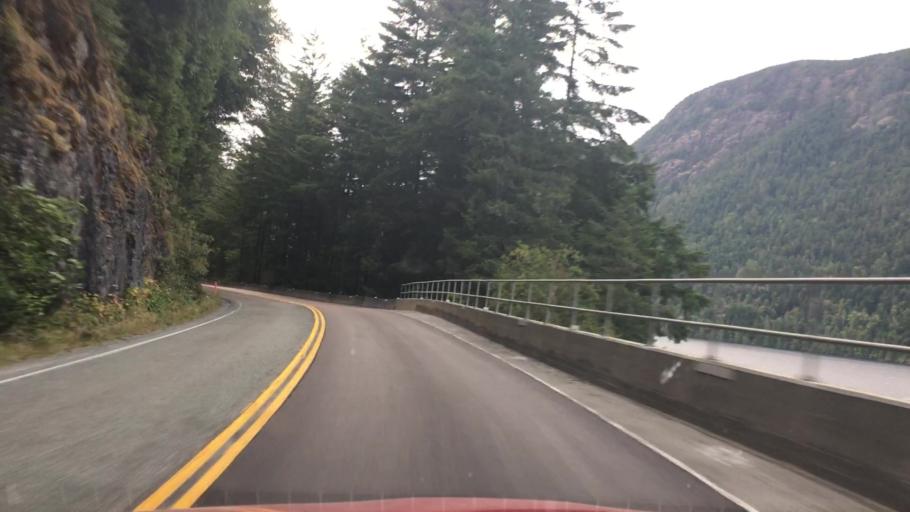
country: CA
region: British Columbia
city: Port Alberni
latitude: 49.2875
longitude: -124.6035
